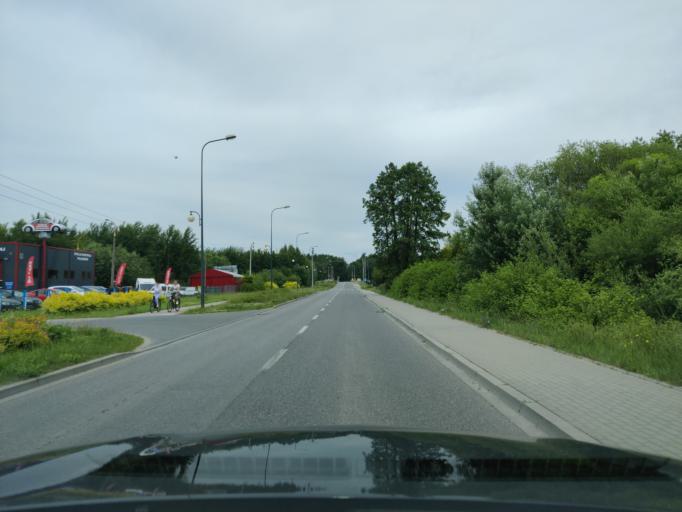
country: PL
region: Masovian Voivodeship
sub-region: Powiat wyszkowski
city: Wyszkow
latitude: 52.6183
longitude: 21.4526
